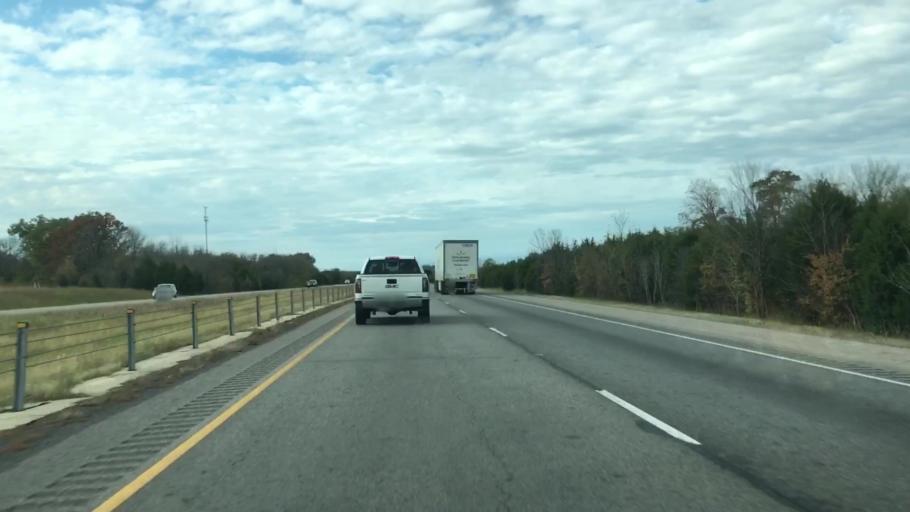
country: US
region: Arkansas
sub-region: Conway County
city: Morrilton
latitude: 35.2004
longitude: -92.8056
